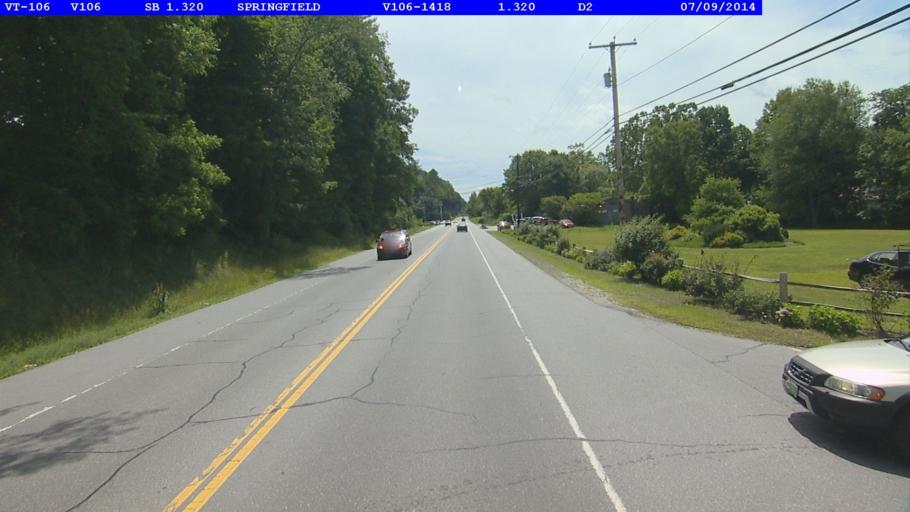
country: US
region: Vermont
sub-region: Windsor County
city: Springfield
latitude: 43.3198
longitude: -72.5056
